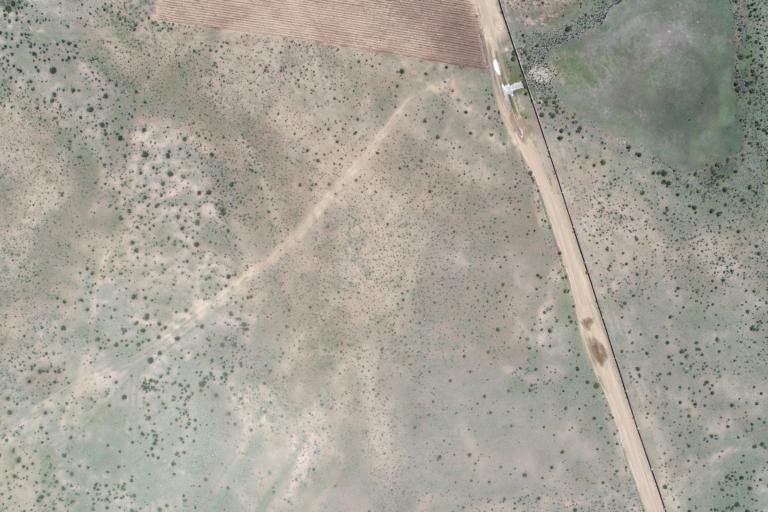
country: BO
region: La Paz
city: Curahuara de Carangas
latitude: -17.2784
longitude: -68.5152
